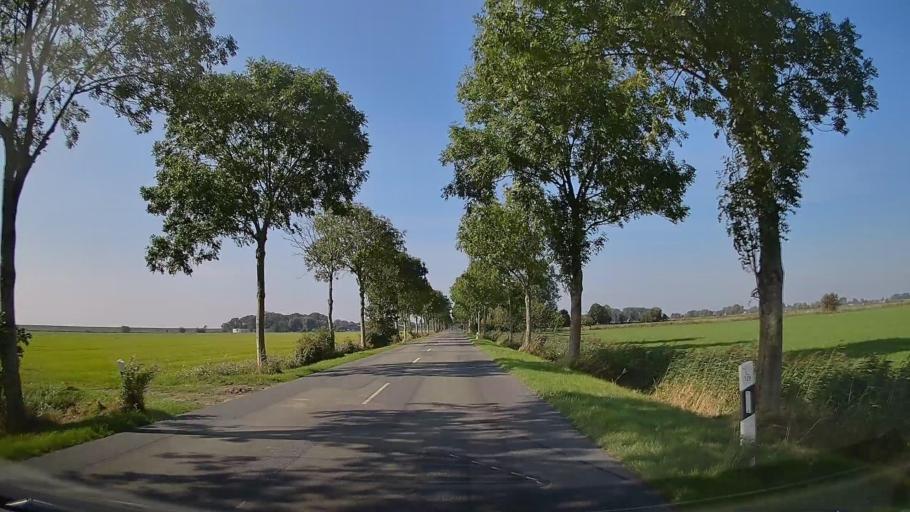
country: DE
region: Lower Saxony
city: Wremen
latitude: 53.6259
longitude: 8.5243
